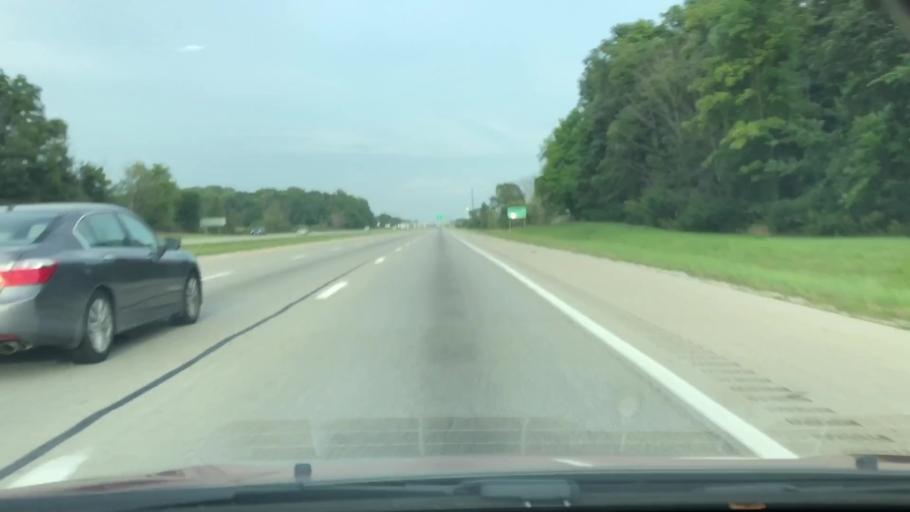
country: US
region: Ohio
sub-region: Clark County
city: Lisbon
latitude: 39.9339
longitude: -83.6321
